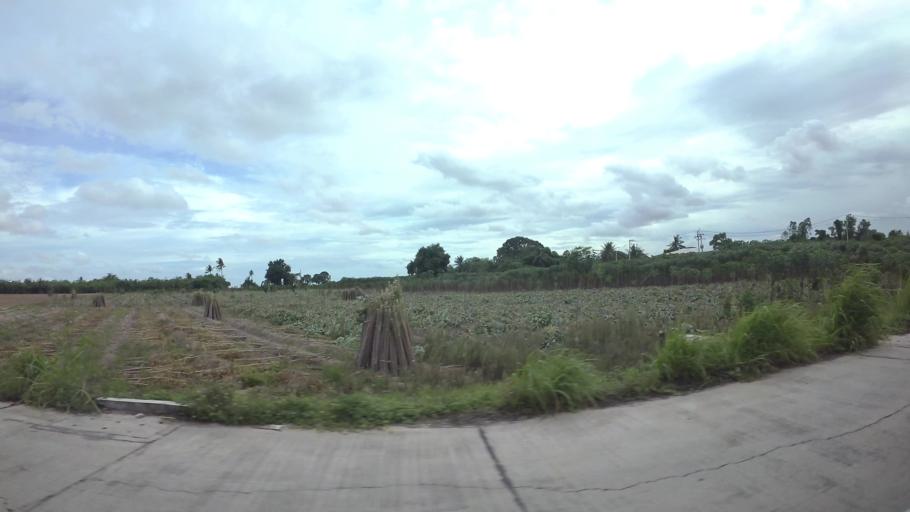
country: TH
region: Chon Buri
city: Si Racha
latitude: 13.1408
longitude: 100.9810
